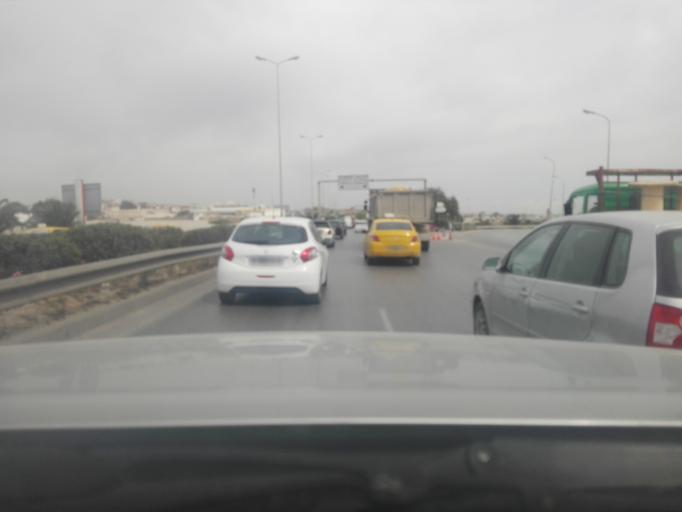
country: TN
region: Bin 'Arus
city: Ben Arous
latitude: 36.7582
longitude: 10.2003
